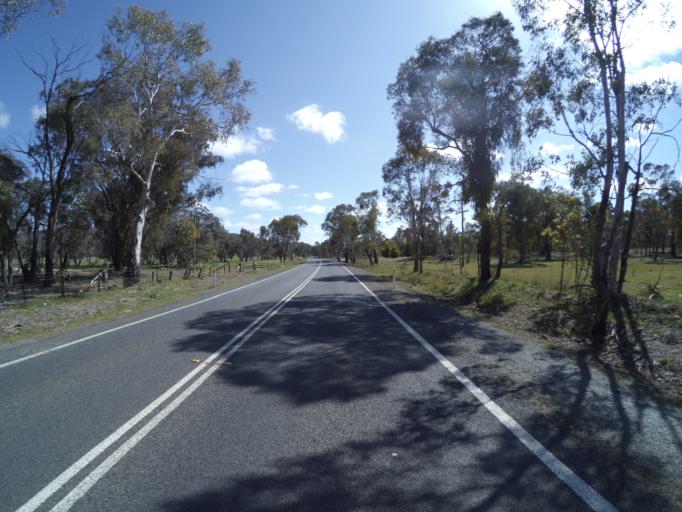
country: AU
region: New South Wales
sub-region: Queanbeyan
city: Queanbeyan
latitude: -35.2518
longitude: 149.2622
